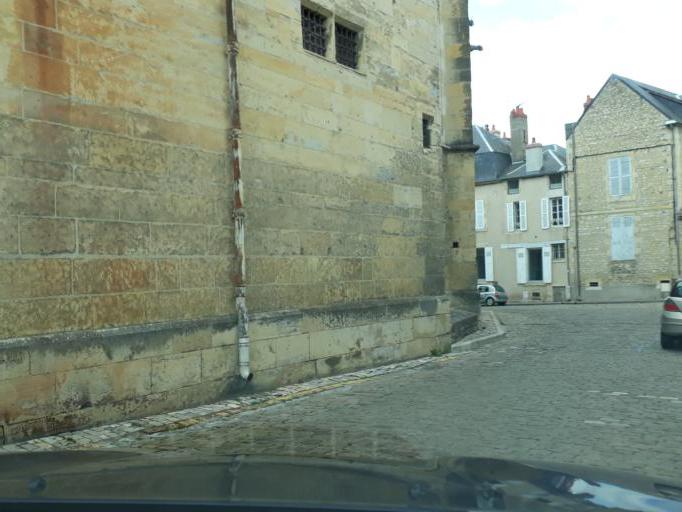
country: FR
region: Bourgogne
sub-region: Departement de la Nievre
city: Nevers
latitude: 46.9870
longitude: 3.1577
